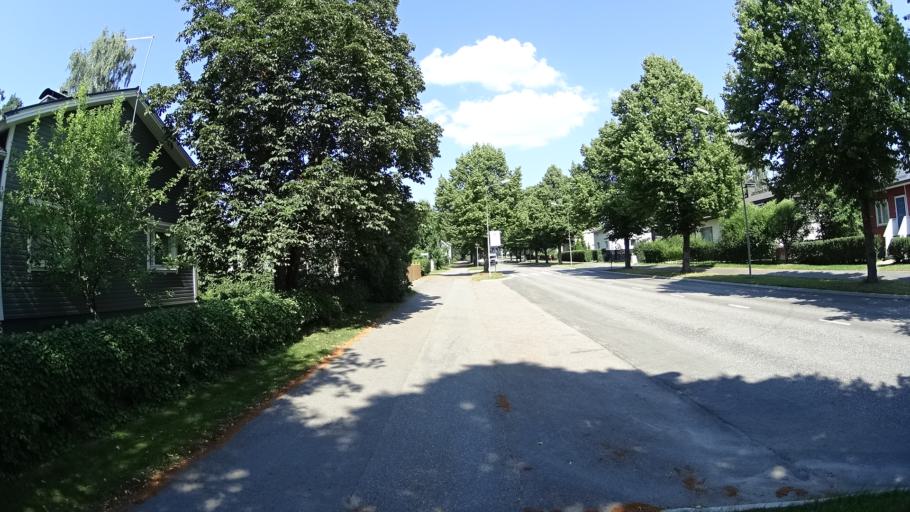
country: FI
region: Uusimaa
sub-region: Porvoo
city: Porvoo
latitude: 60.3966
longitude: 25.6806
